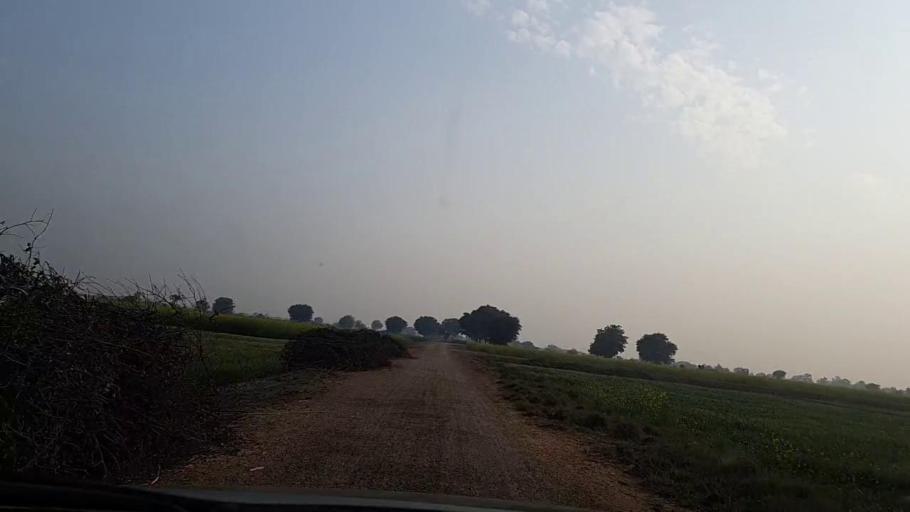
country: PK
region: Sindh
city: Nawabshah
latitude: 26.2712
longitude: 68.3235
